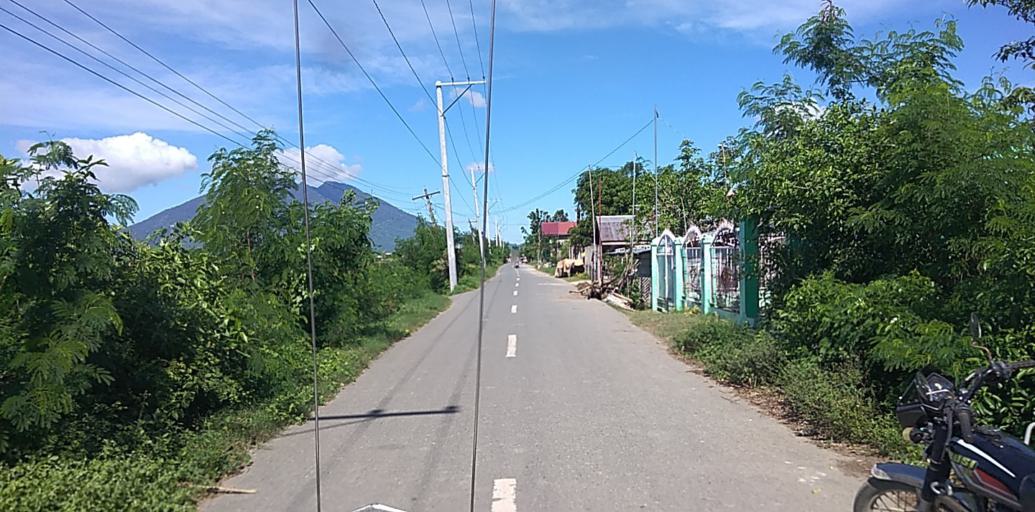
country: PH
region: Central Luzon
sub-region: Province of Pampanga
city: Candating
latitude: 15.1301
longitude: 120.8086
